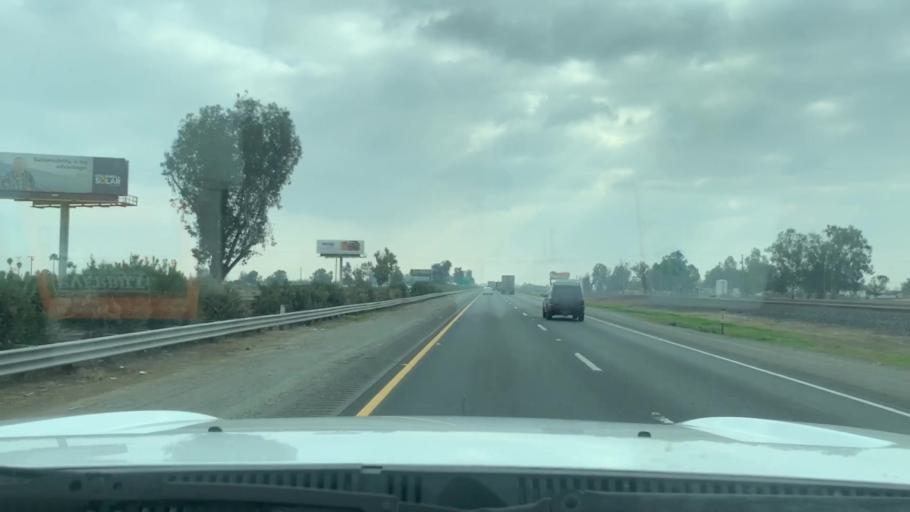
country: US
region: California
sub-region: Tulare County
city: Pixley
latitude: 35.9954
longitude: -119.2999
